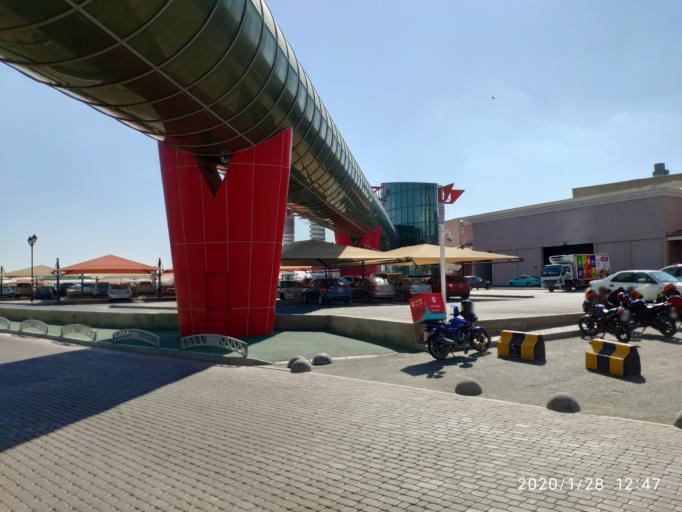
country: QA
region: Baladiyat ar Rayyan
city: Ar Rayyan
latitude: 25.2620
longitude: 51.4445
